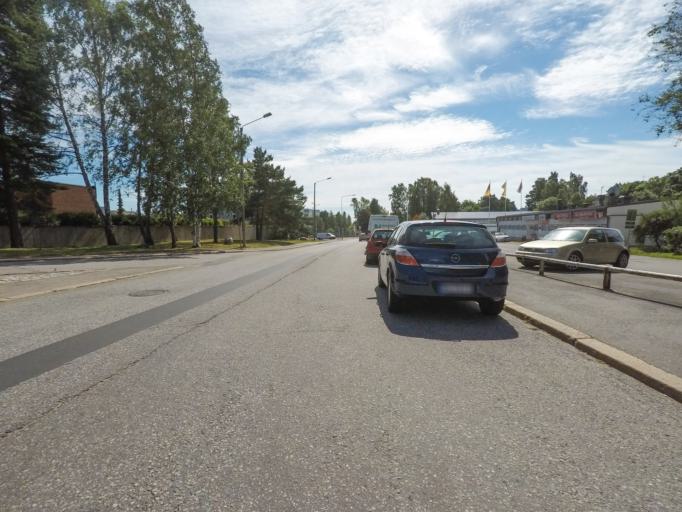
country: FI
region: Uusimaa
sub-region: Helsinki
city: Vantaa
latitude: 60.2029
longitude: 25.0595
